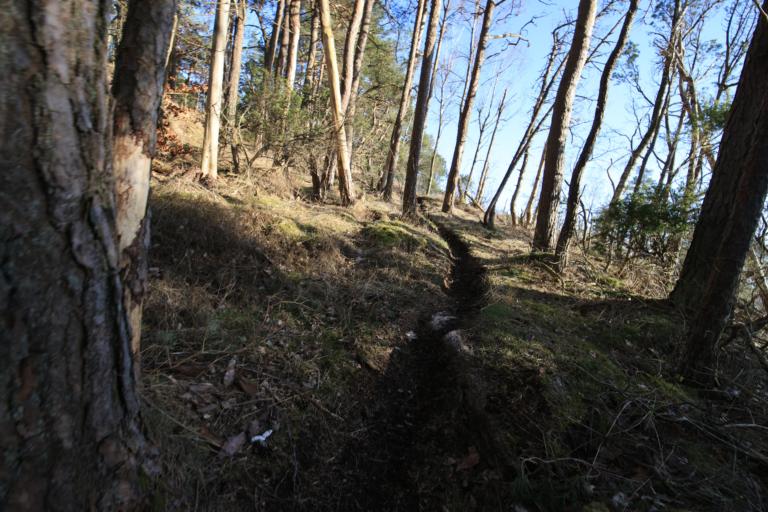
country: SE
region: Halland
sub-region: Varbergs Kommun
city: Varberg
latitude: 57.1662
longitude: 12.2648
